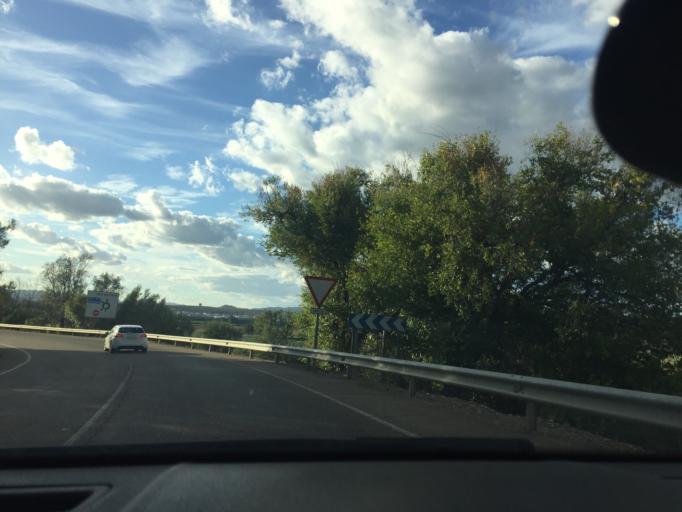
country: ES
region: Andalusia
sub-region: Province of Cordoba
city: El Carpio
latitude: 37.9533
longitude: -4.5134
